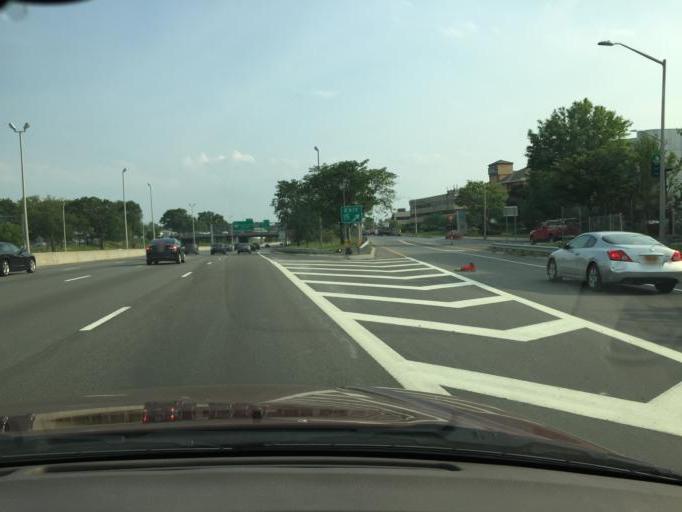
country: US
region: New York
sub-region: Bronx
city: The Bronx
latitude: 40.7843
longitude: -73.8247
